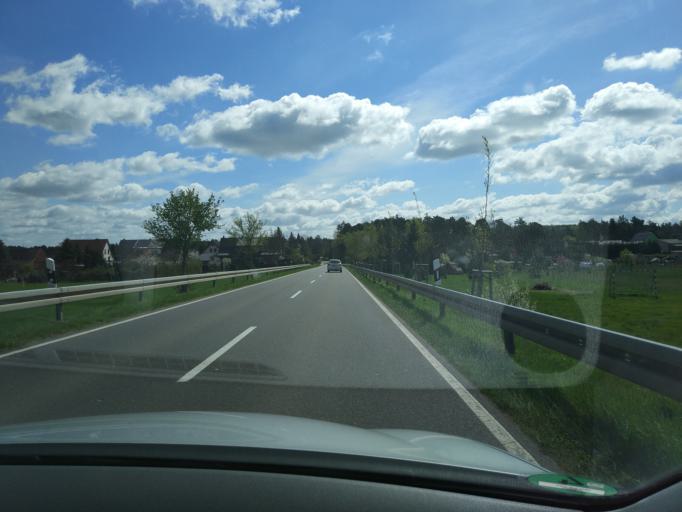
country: DE
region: Saxony-Anhalt
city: Oranienbaum
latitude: 51.7936
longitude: 12.4185
